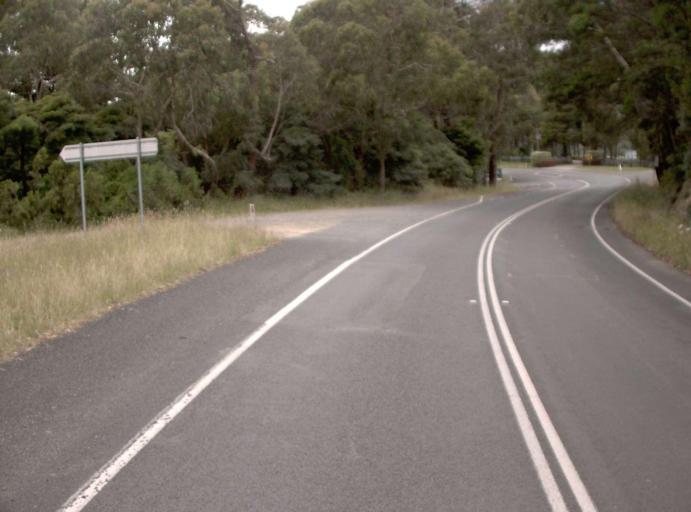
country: AU
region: Victoria
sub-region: Yarra Ranges
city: Healesville
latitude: -37.6474
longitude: 145.5497
